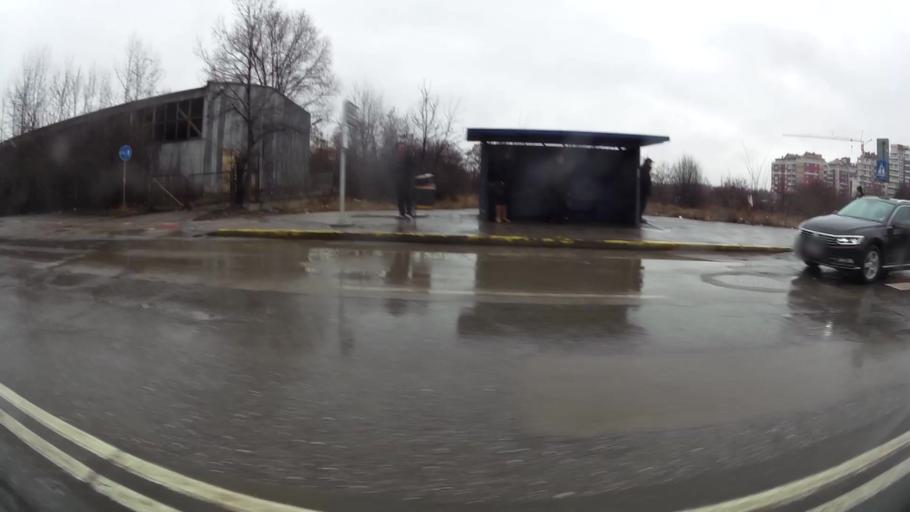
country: BG
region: Sofia-Capital
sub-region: Stolichna Obshtina
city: Sofia
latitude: 42.6324
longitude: 23.3803
